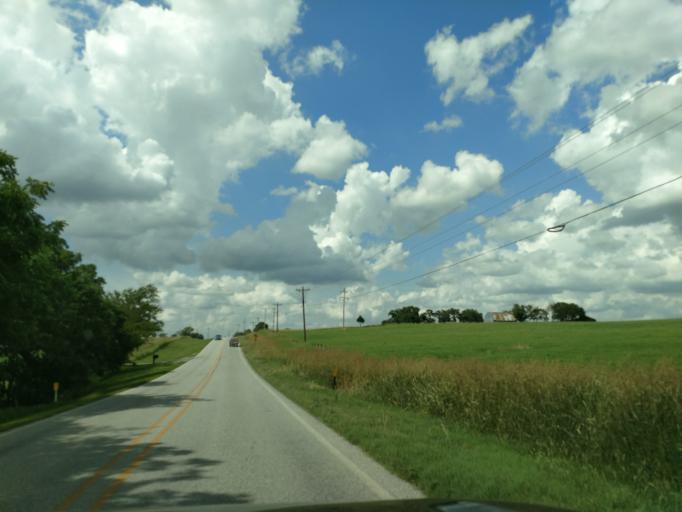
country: US
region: Arkansas
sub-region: Carroll County
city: Berryville
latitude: 36.4659
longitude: -93.5557
